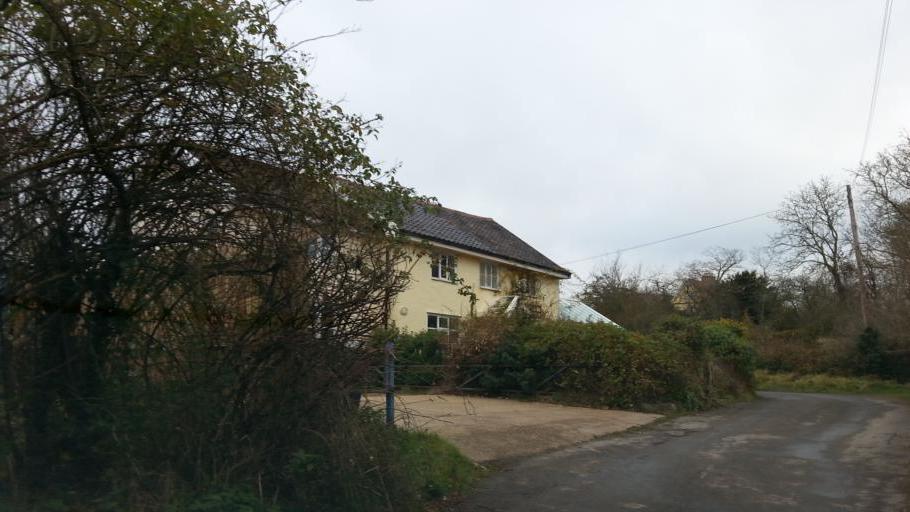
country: GB
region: England
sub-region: Suffolk
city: Cookley
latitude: 52.3029
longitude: 1.3671
